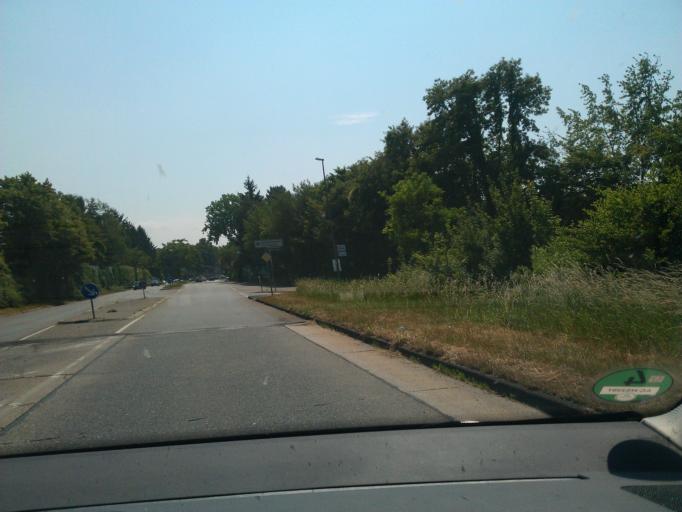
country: DE
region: Hesse
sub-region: Regierungsbezirk Darmstadt
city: Wiesbaden
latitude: 50.0877
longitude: 8.2782
